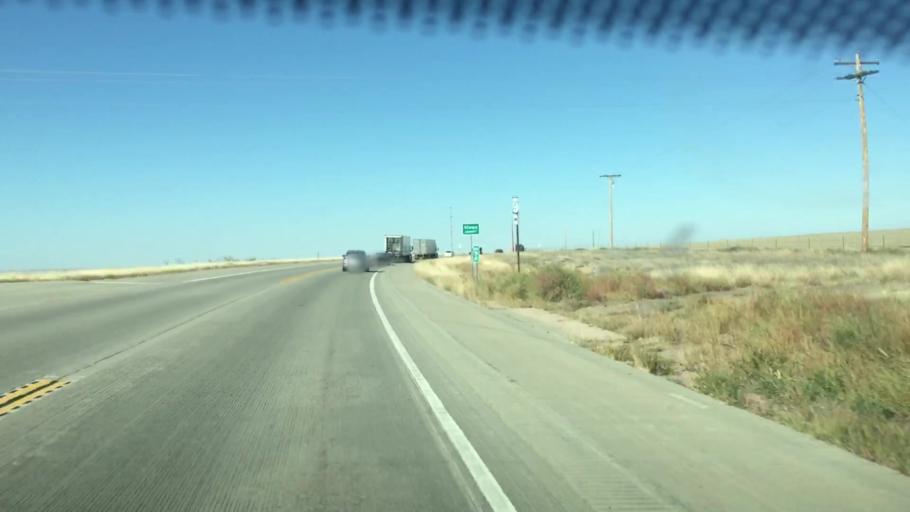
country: US
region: Colorado
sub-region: Prowers County
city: Lamar
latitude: 38.2671
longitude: -102.7237
